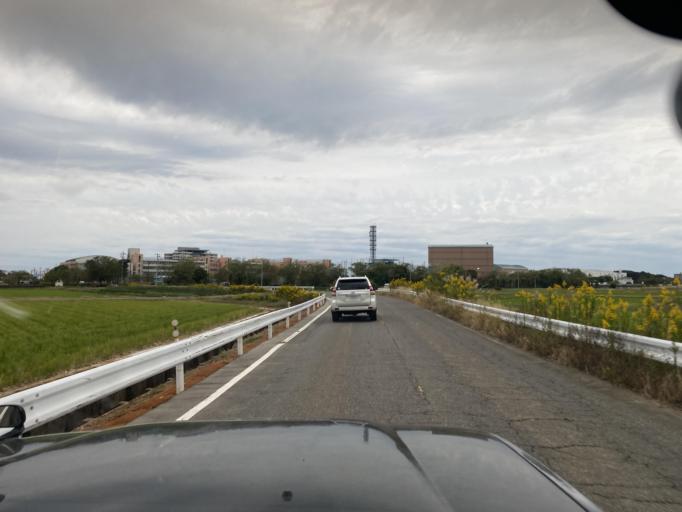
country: JP
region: Niigata
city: Niigata-shi
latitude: 37.8748
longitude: 139.0509
